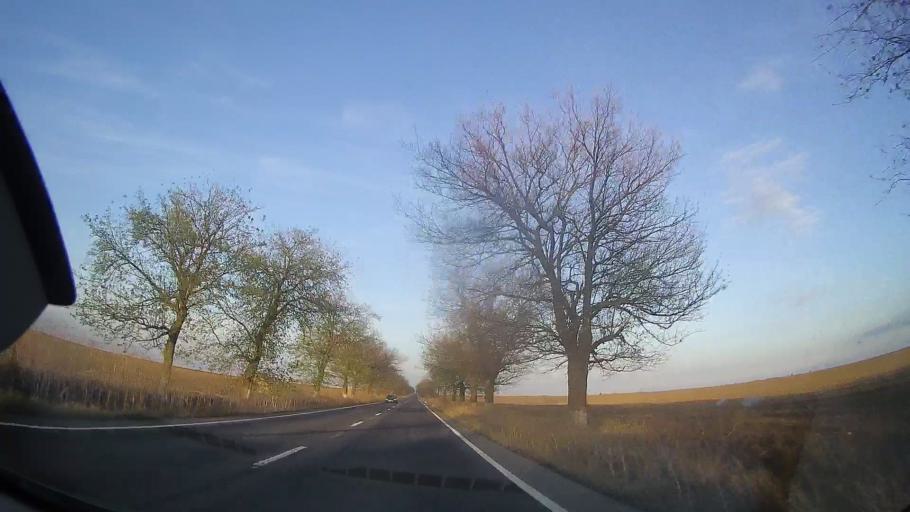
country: RO
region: Constanta
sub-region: Comuna Comana
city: Comana
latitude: 43.9052
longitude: 28.3309
